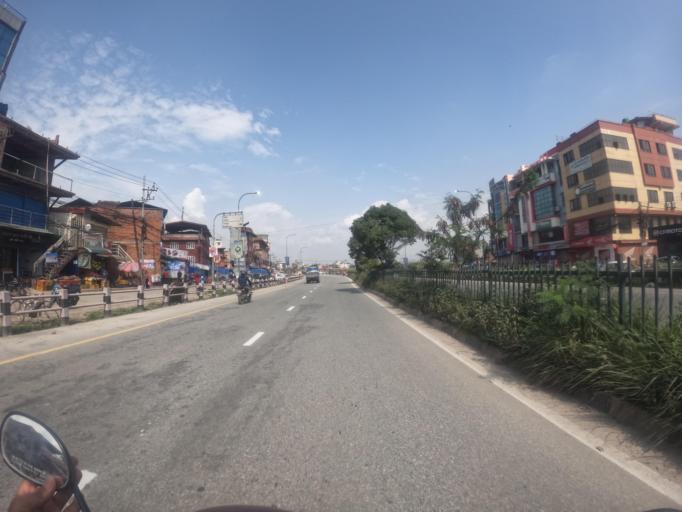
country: NP
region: Central Region
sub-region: Bagmati Zone
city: Bhaktapur
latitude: 27.6709
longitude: 85.4095
